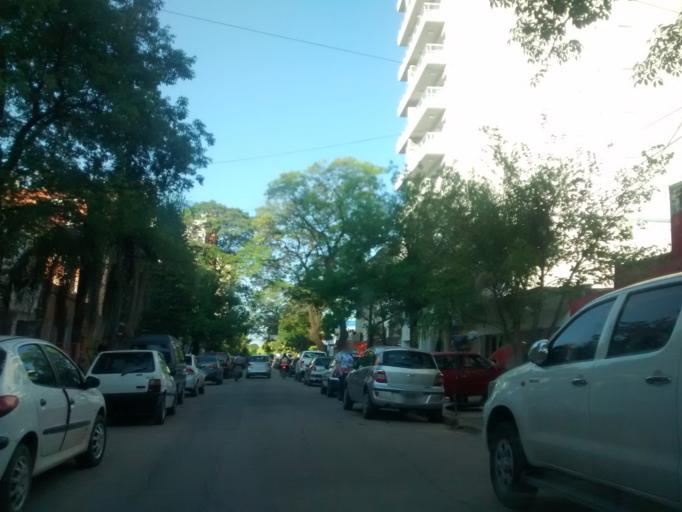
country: AR
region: Chaco
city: Resistencia
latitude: -27.4586
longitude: -58.9844
